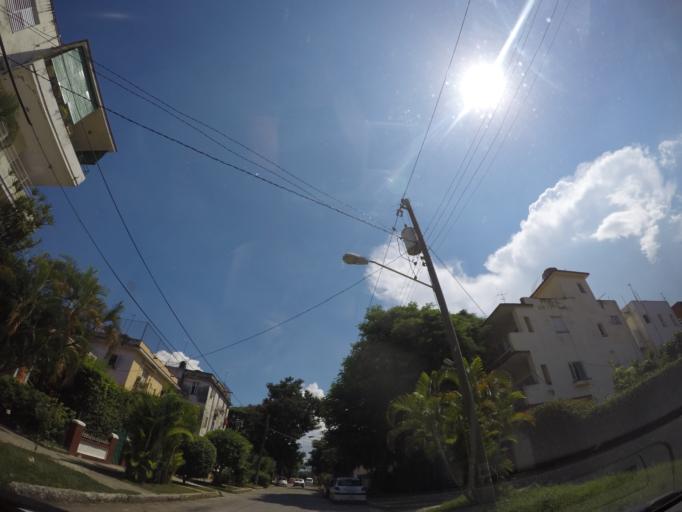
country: CU
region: La Habana
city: Havana
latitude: 23.1269
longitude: -82.4052
